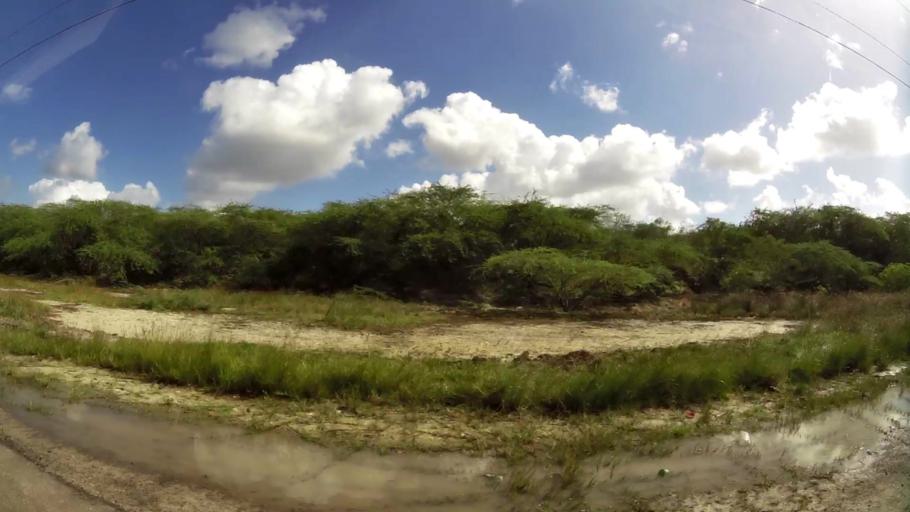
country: AG
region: Saint John
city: Saint John's
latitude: 17.1345
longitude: -61.8607
